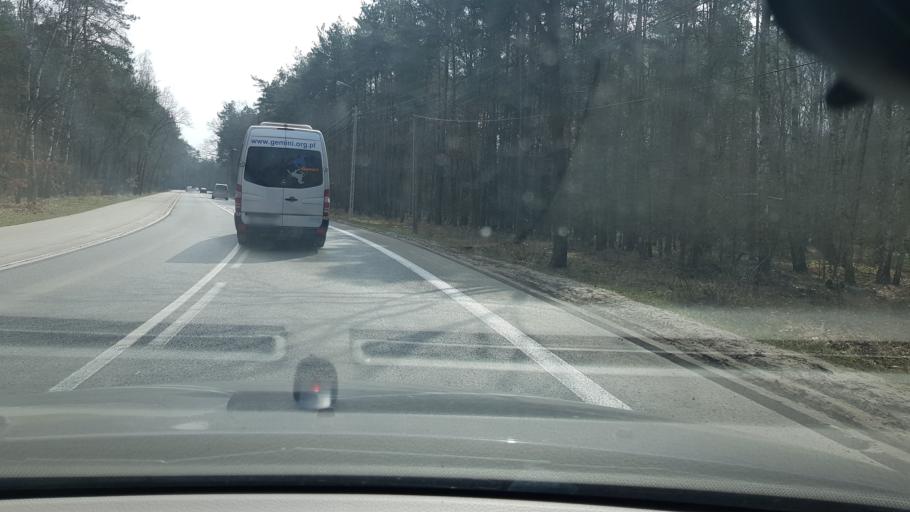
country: PL
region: Masovian Voivodeship
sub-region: Warszawa
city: Wesola
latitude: 52.2364
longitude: 21.2220
